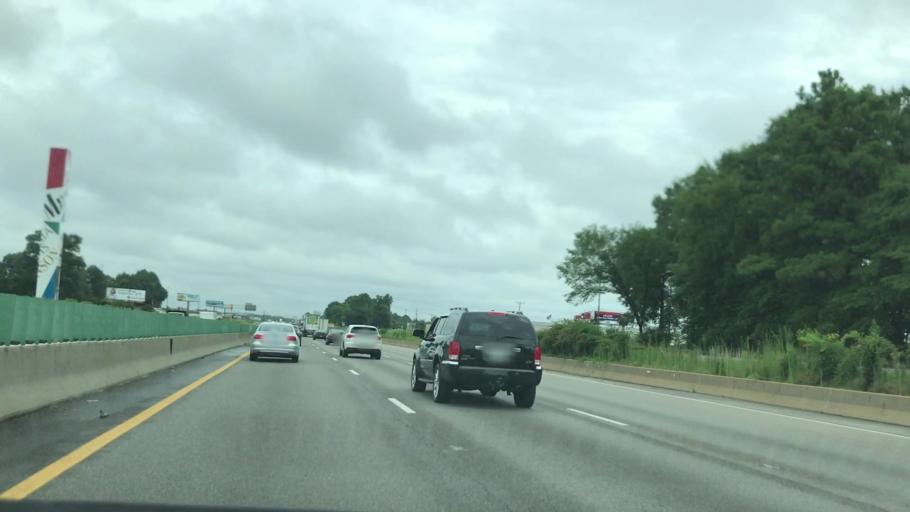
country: US
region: Virginia
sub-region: Chesterfield County
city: Bensley
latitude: 37.4725
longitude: -77.4289
